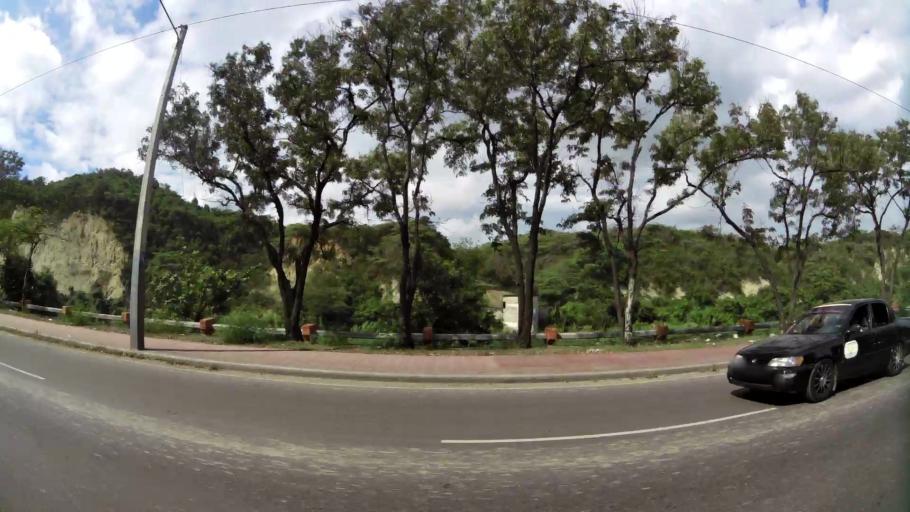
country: DO
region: Santiago
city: Santiago de los Caballeros
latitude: 19.4509
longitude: -70.7143
